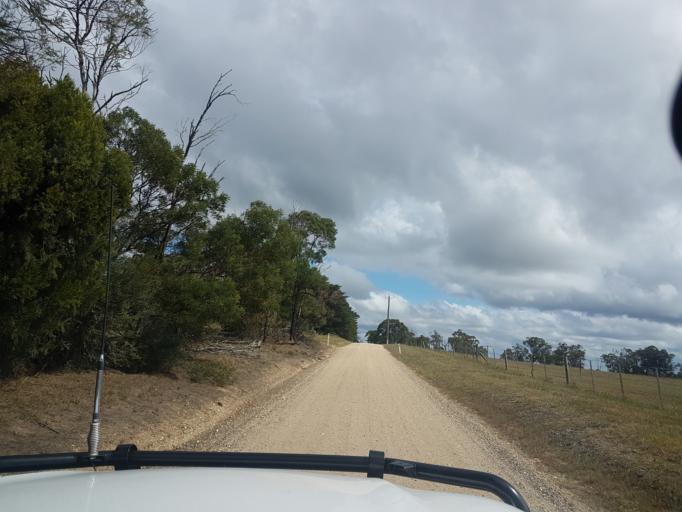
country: AU
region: Victoria
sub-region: East Gippsland
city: Bairnsdale
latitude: -37.7838
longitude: 147.5271
